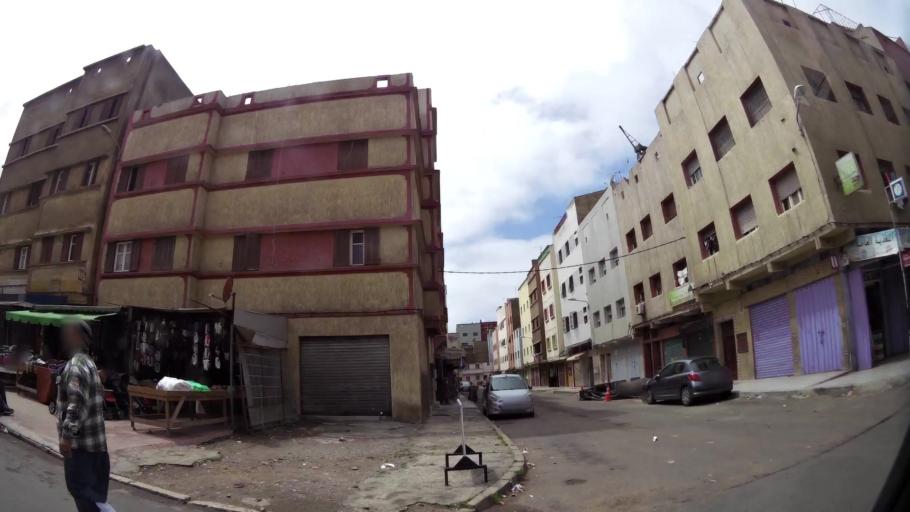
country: MA
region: Grand Casablanca
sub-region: Mediouna
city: Tit Mellil
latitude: 33.6060
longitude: -7.5122
